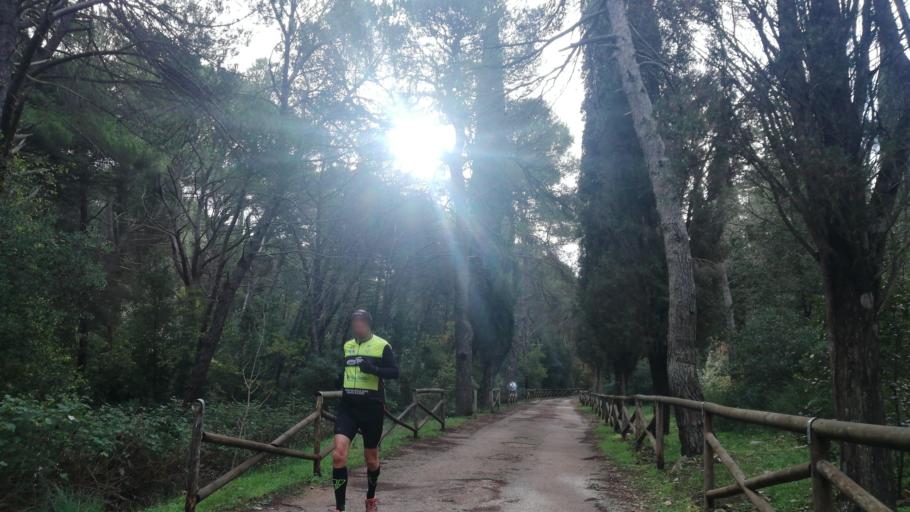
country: IT
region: Apulia
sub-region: Provincia di Bari
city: Cassano delle Murge
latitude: 40.8887
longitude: 16.7007
